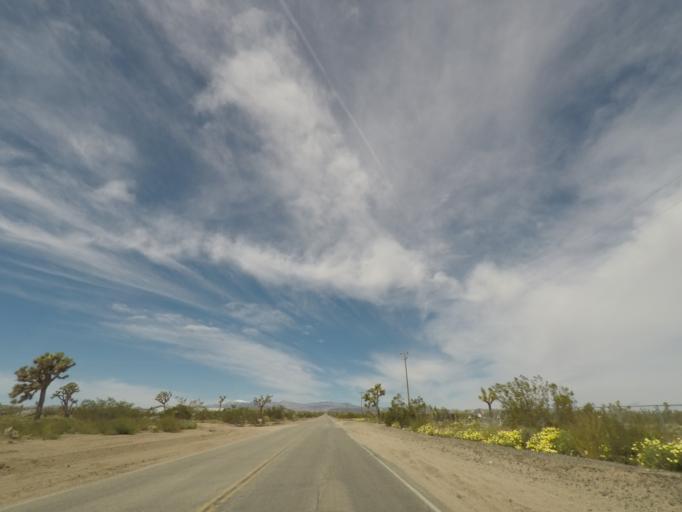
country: US
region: California
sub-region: San Bernardino County
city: Joshua Tree
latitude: 34.1931
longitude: -116.3512
